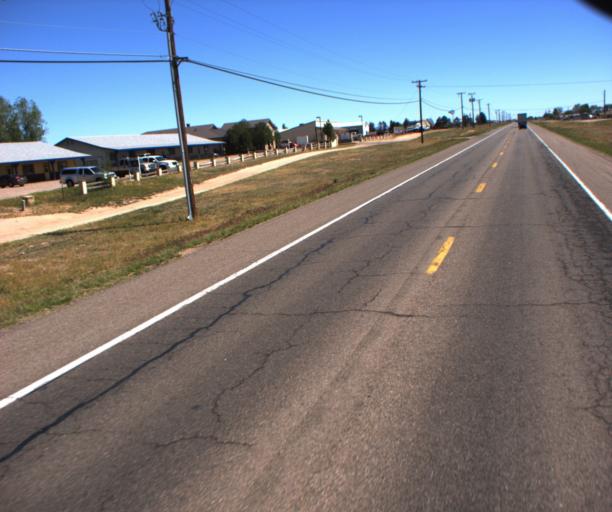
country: US
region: Arizona
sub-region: Yavapai County
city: Chino Valley
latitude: 34.8000
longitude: -112.4506
